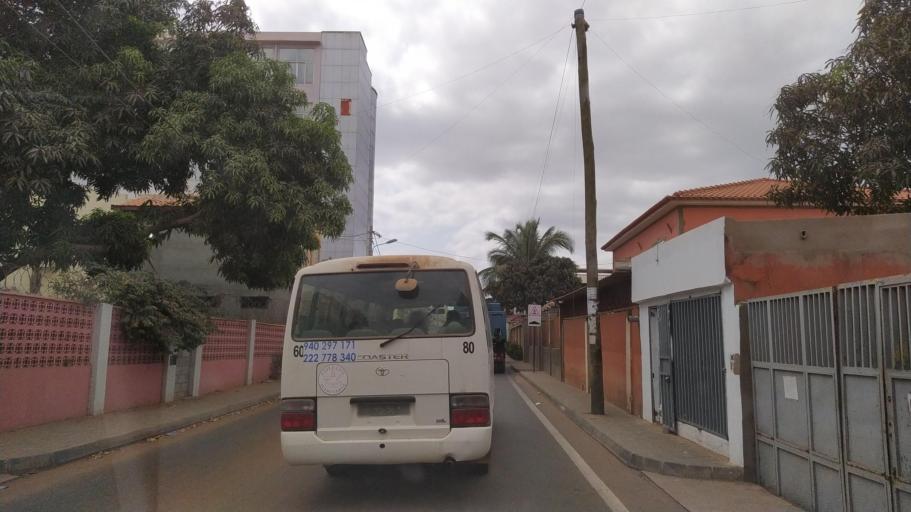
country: AO
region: Luanda
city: Luanda
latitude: -8.9652
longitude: 13.1534
